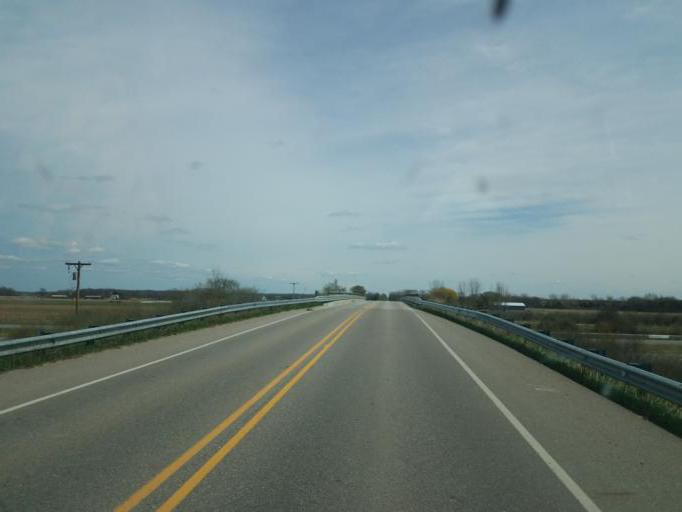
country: US
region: Michigan
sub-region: Isabella County
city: Mount Pleasant
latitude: 43.6406
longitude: -84.7599
